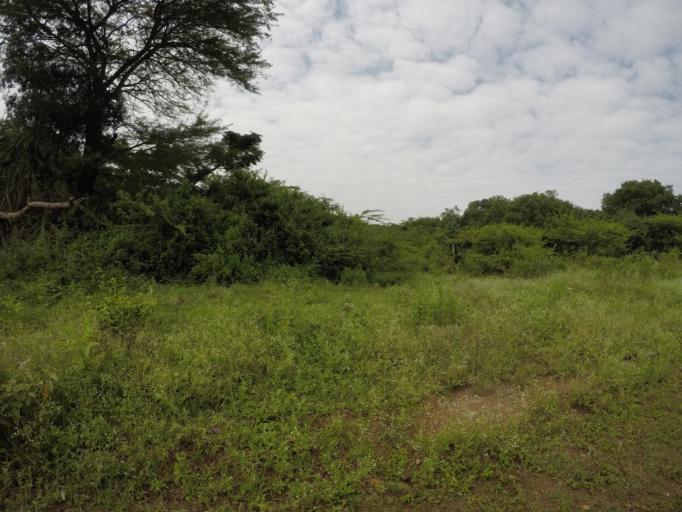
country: ZA
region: KwaZulu-Natal
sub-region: uThungulu District Municipality
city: Empangeni
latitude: -28.6278
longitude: 31.8939
